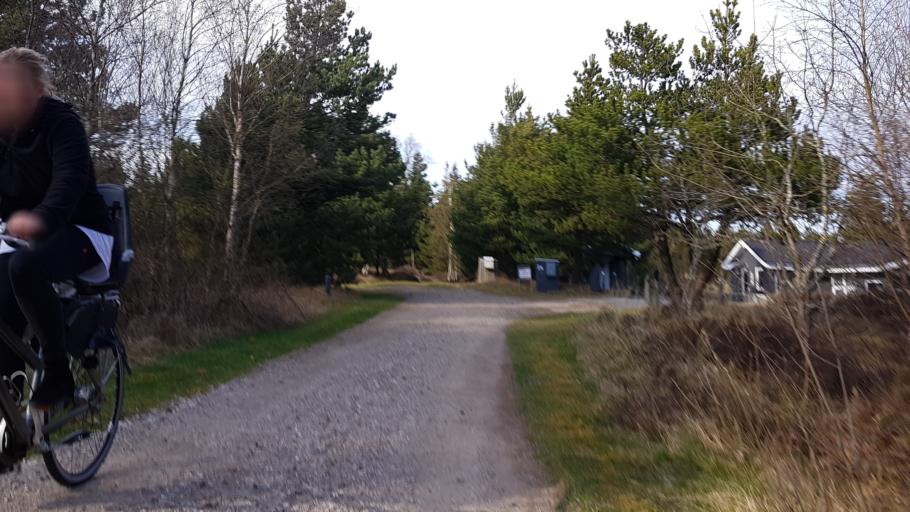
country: DE
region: Schleswig-Holstein
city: List
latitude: 55.1296
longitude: 8.5381
